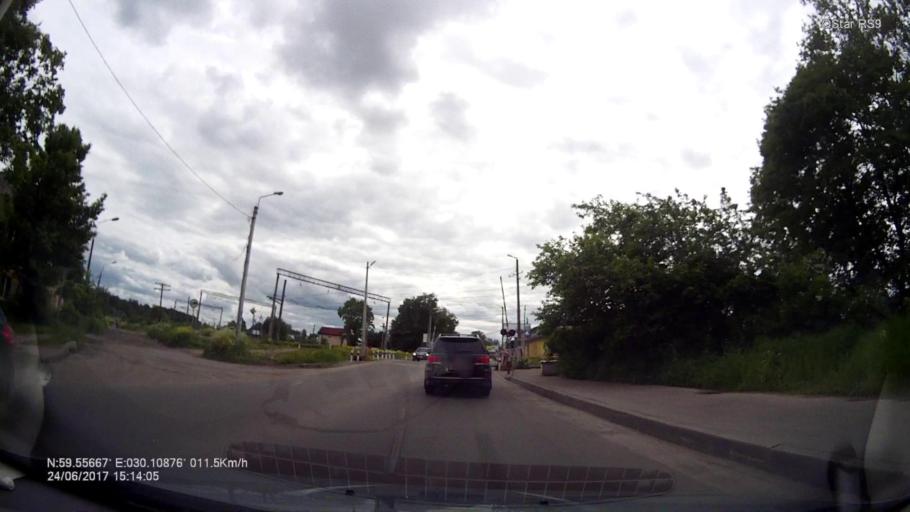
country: RU
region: Leningrad
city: Gatchina
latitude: 59.5567
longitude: 30.1088
